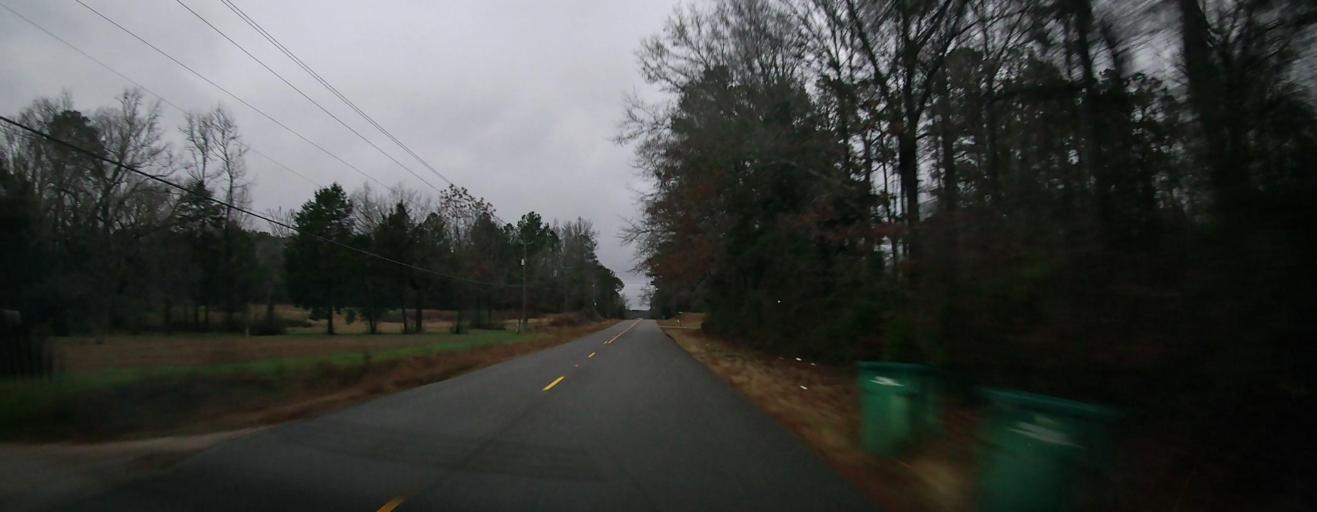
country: US
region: Alabama
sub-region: Tuscaloosa County
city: Vance
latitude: 33.1470
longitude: -87.2298
